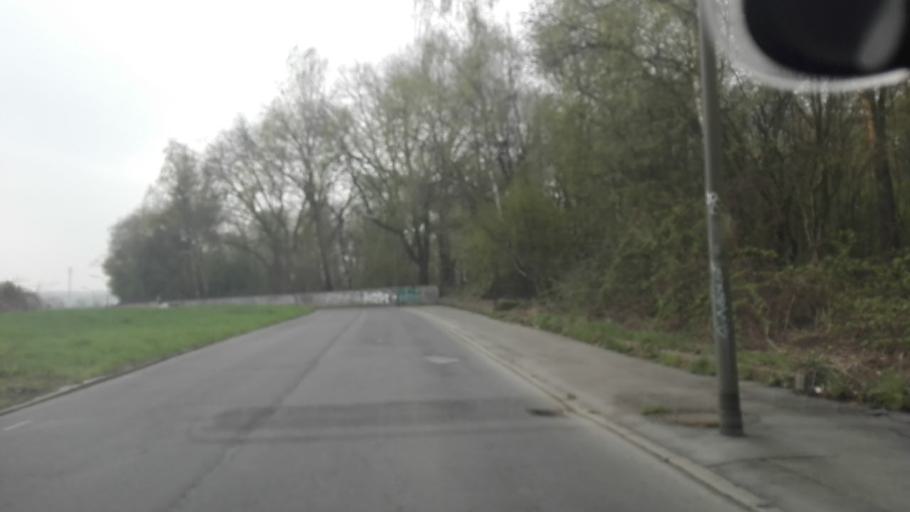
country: DE
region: North Rhine-Westphalia
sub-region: Regierungsbezirk Arnsberg
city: Dortmund
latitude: 51.4689
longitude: 7.4259
